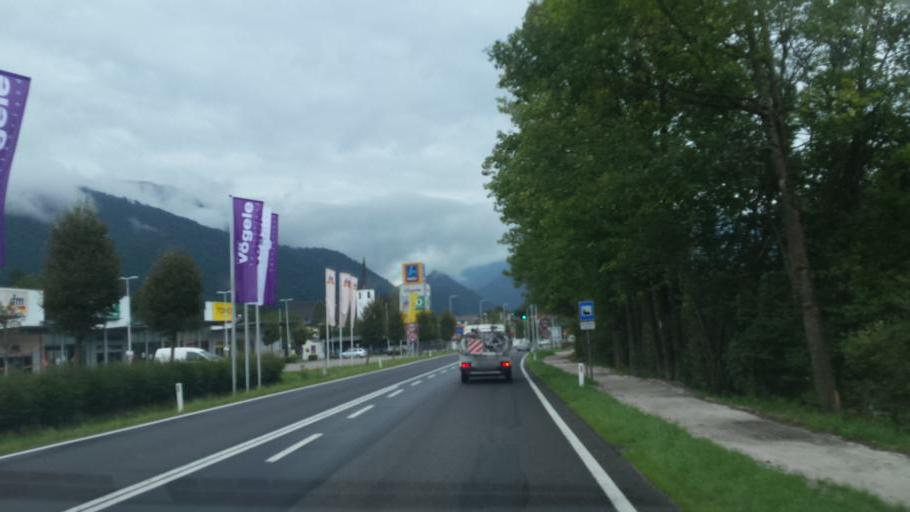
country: AT
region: Upper Austria
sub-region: Politischer Bezirk Gmunden
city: Bad Ischl
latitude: 47.7179
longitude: 13.5826
